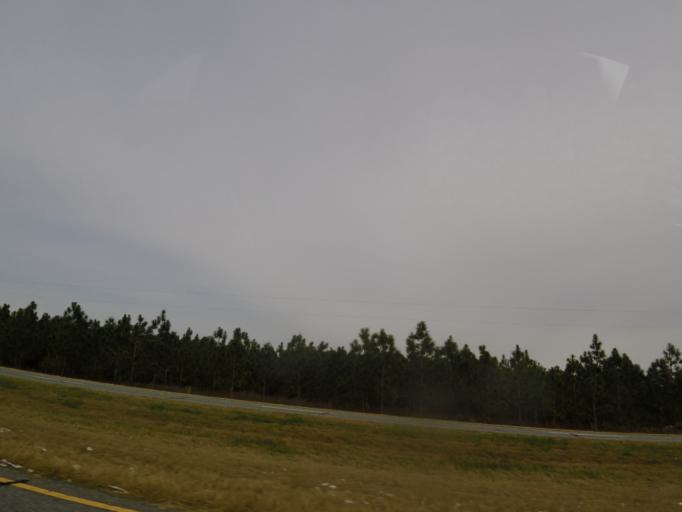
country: US
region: Georgia
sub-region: Seminole County
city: Donalsonville
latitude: 30.9866
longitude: -84.7575
